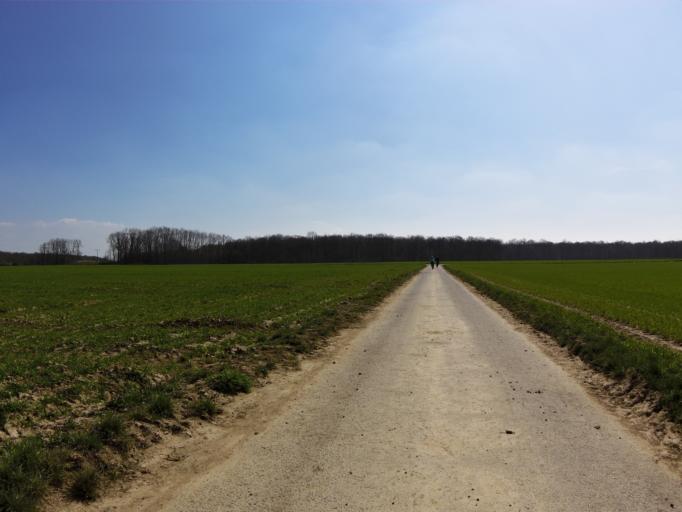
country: DE
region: Bavaria
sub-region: Regierungsbezirk Unterfranken
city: Sulzfeld am Main
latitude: 49.7261
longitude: 10.0978
